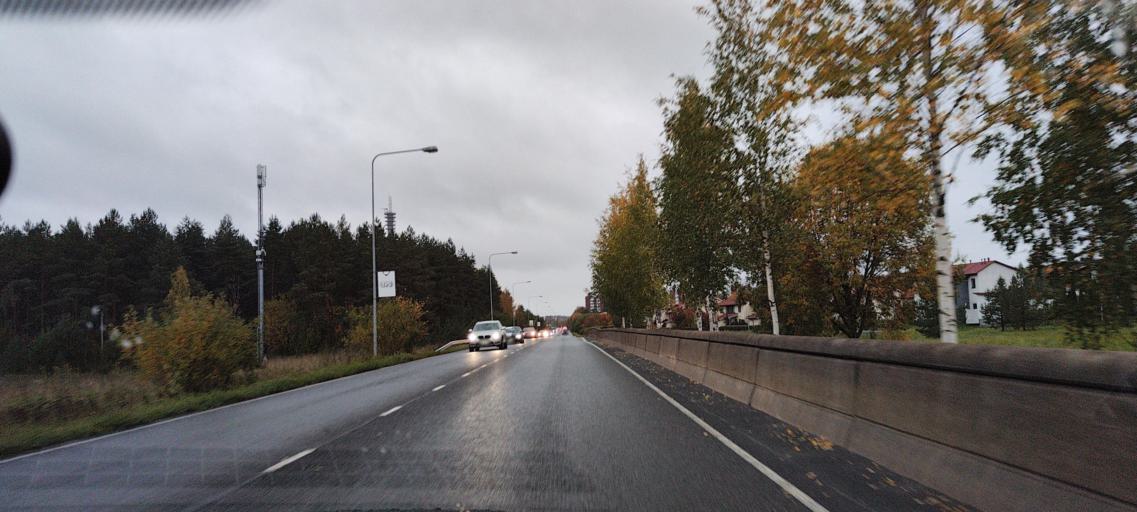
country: FI
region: Varsinais-Suomi
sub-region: Turku
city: Kaarina
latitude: 60.4557
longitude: 22.3337
